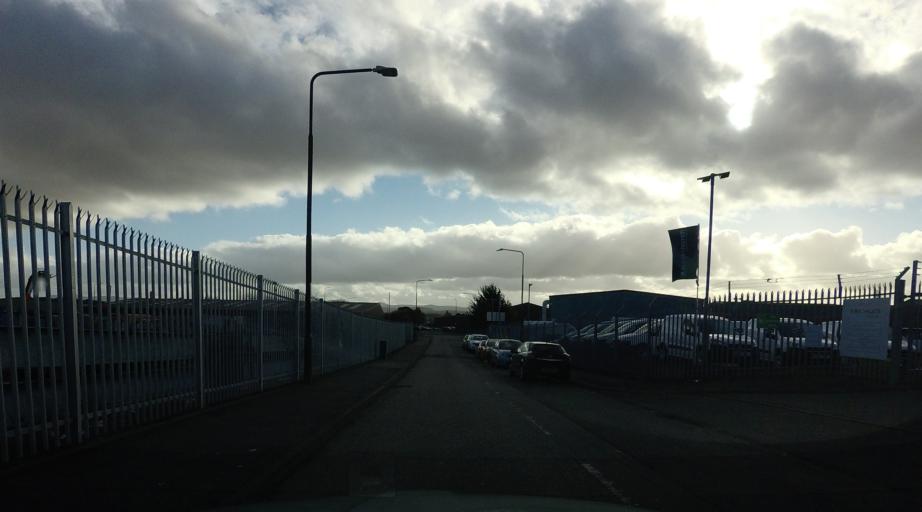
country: GB
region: Scotland
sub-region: West Lothian
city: Broxburn
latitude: 55.9414
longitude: -3.4563
